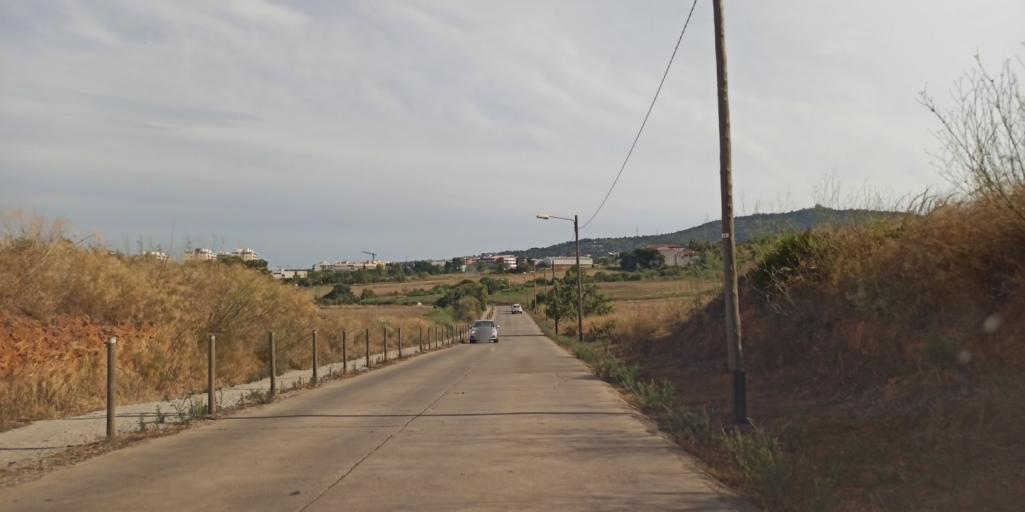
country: ES
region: Catalonia
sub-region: Provincia de Barcelona
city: Santa Coloma de Cervello
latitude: 41.3630
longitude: 2.0238
